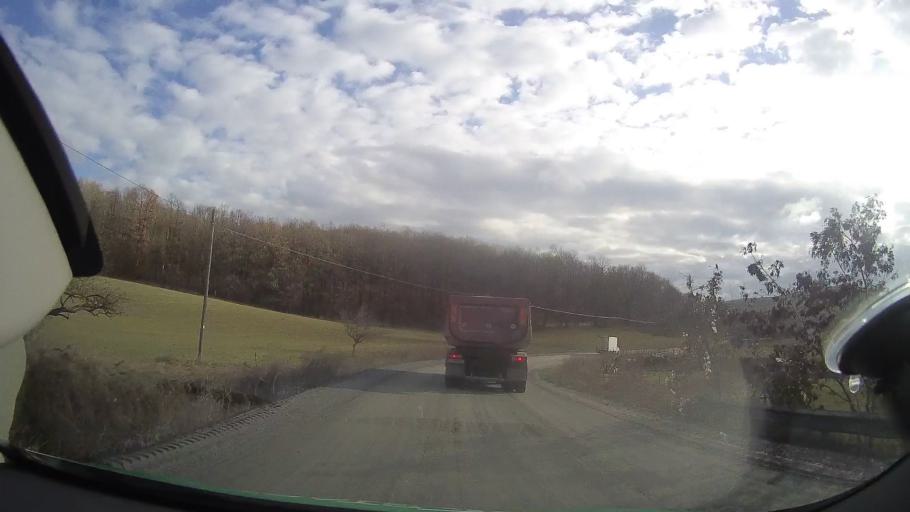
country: RO
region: Cluj
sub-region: Comuna Savadisla
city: Savadisla
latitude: 46.6472
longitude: 23.4624
